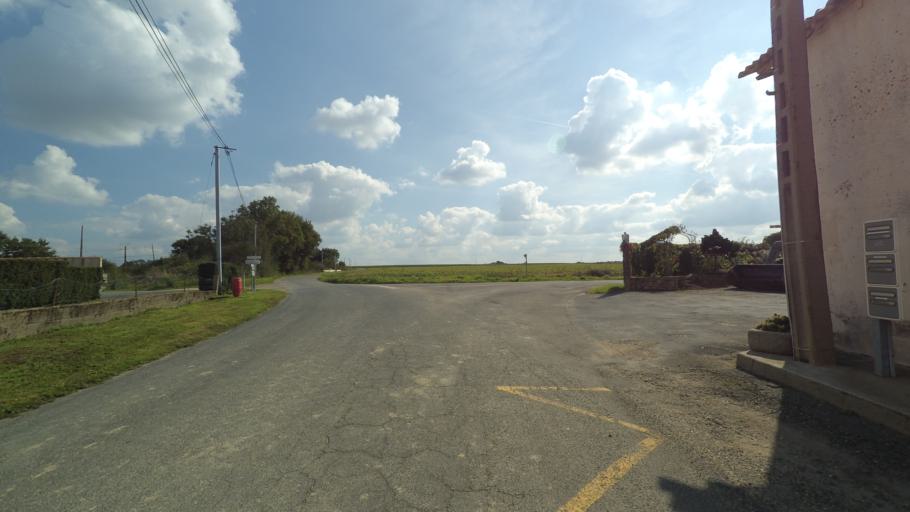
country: FR
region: Pays de la Loire
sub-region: Departement de la Vendee
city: Bouffere
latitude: 46.9584
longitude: -1.3802
